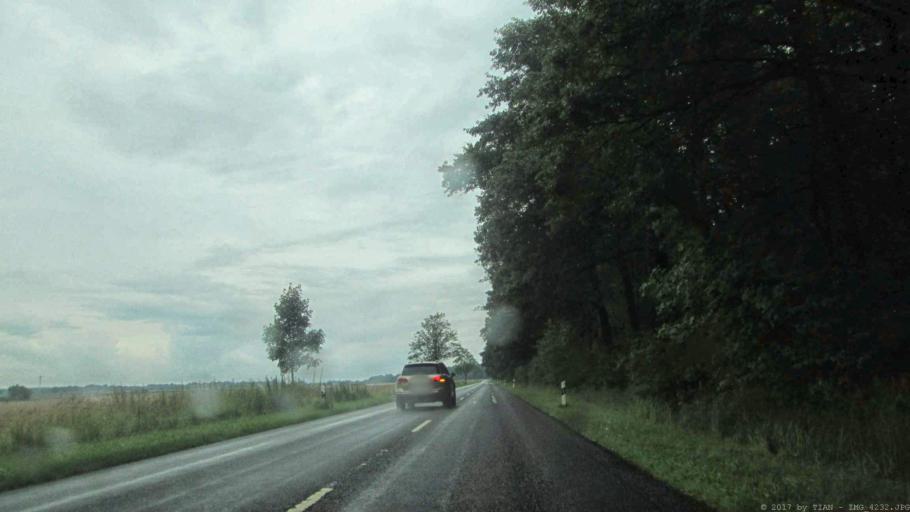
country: DE
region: Lower Saxony
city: Danndorf
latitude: 52.4182
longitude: 10.8868
